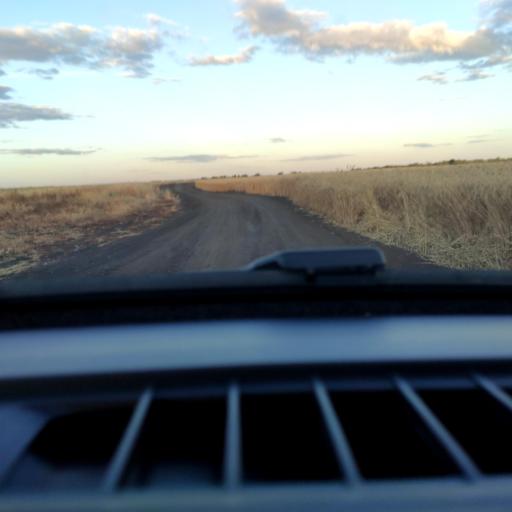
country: RU
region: Voronezj
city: Verkhnyaya Khava
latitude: 51.6110
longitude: 39.8213
